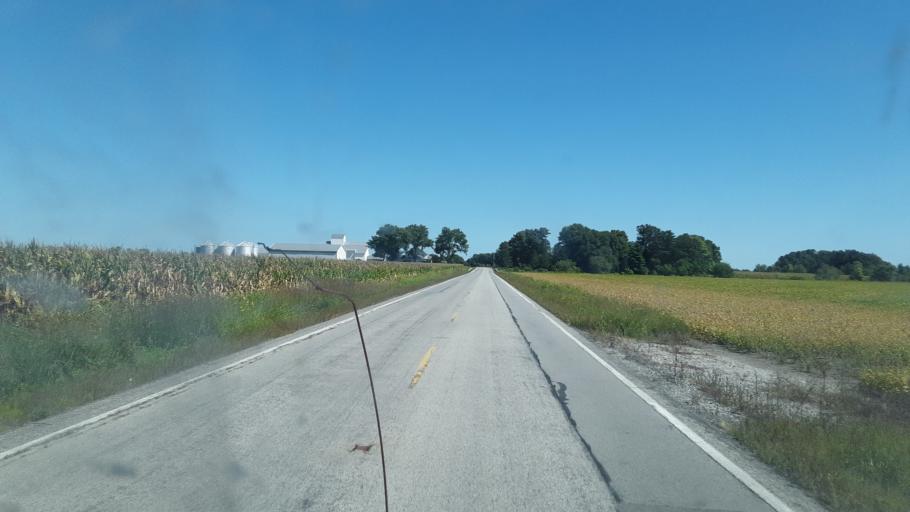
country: US
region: Ohio
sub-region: Huron County
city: Monroeville
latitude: 41.2315
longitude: -82.7466
